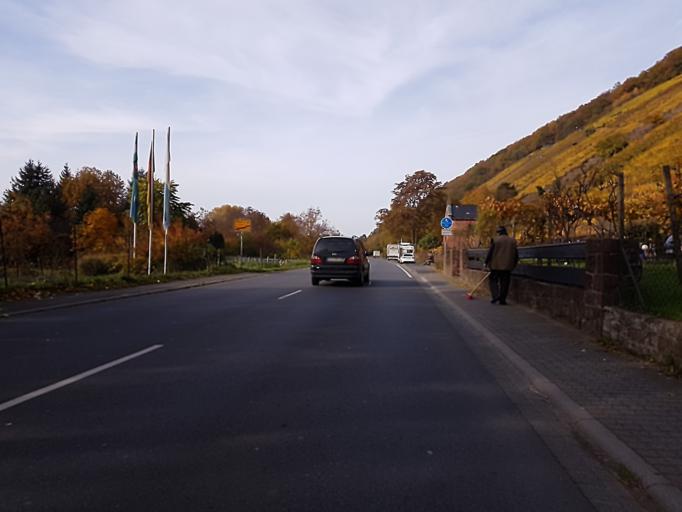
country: DE
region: Bavaria
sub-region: Regierungsbezirk Unterfranken
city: Klingenberg am Main
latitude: 49.7881
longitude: 9.1782
